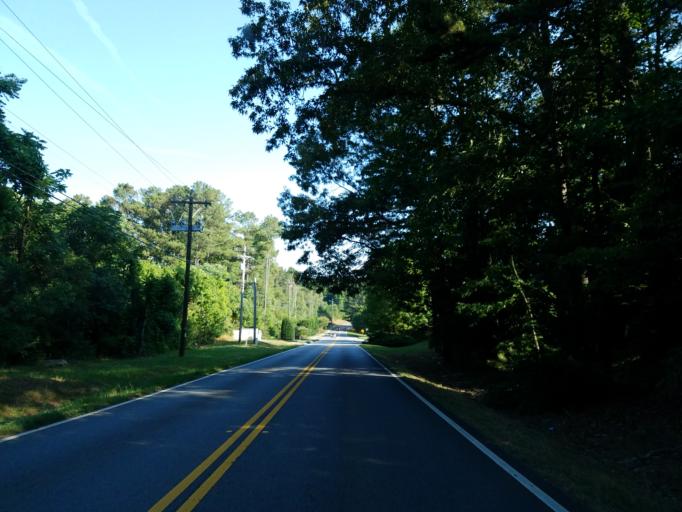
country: US
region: Georgia
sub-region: Fulton County
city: Milton
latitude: 34.1362
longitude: -84.3439
